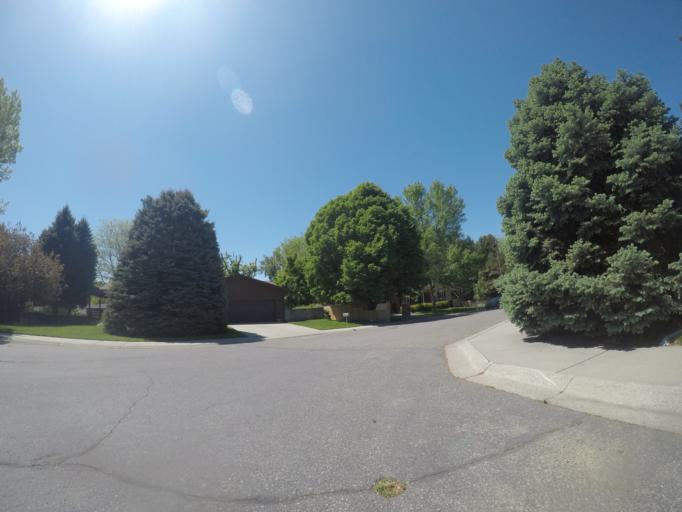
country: US
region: Montana
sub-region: Yellowstone County
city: Billings
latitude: 45.7971
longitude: -108.5667
